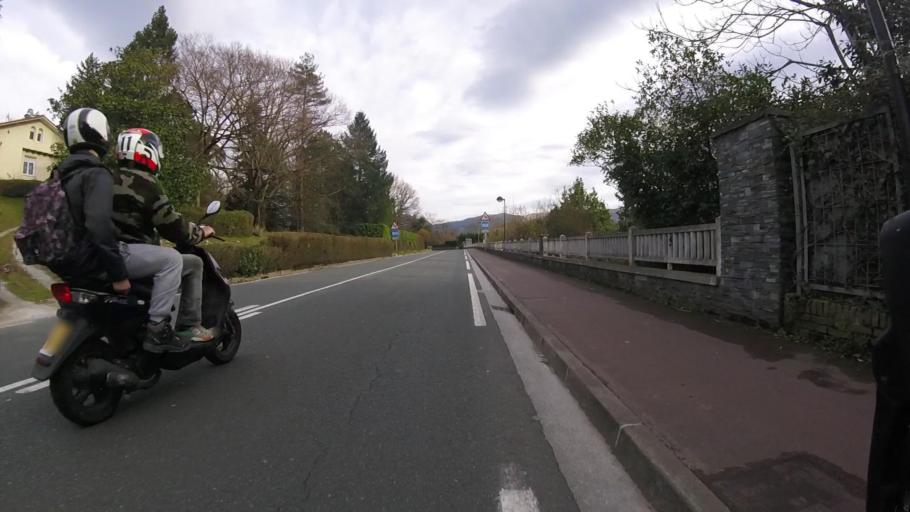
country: ES
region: Basque Country
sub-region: Provincia de Guipuzcoa
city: Lezo
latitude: 43.3026
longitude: -1.8723
